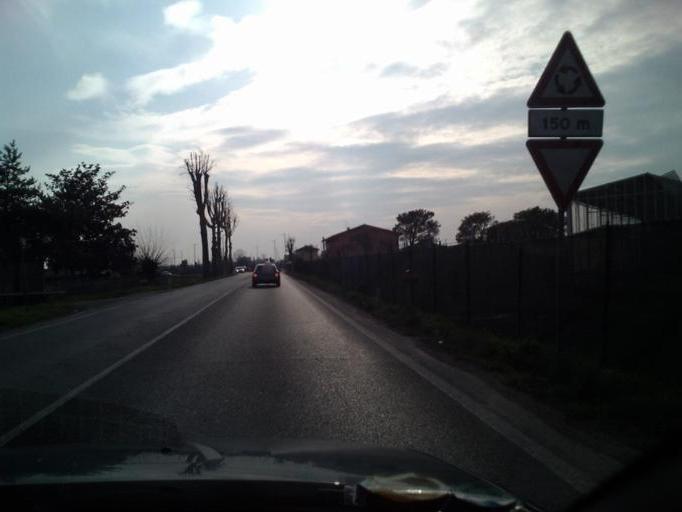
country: IT
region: Veneto
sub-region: Provincia di Verona
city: Povegliano Veronese
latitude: 45.3778
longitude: 10.8834
